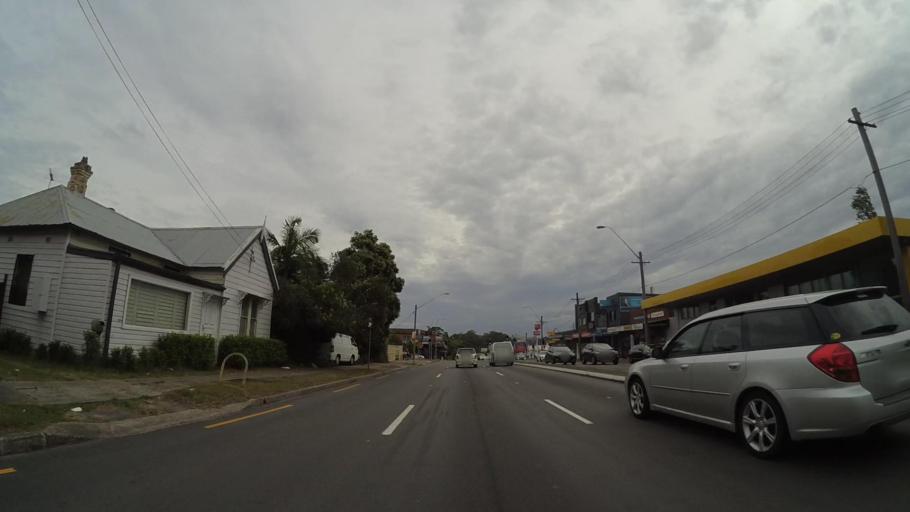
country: AU
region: New South Wales
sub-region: Kogarah
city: Kogarah Bay
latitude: -33.9780
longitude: 151.1234
